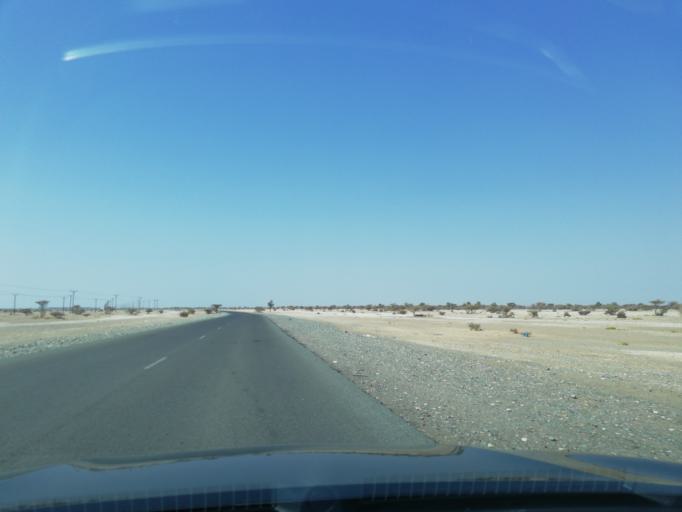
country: OM
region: Muhafazat ad Dakhiliyah
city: Adam
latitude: 22.3411
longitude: 58.0686
